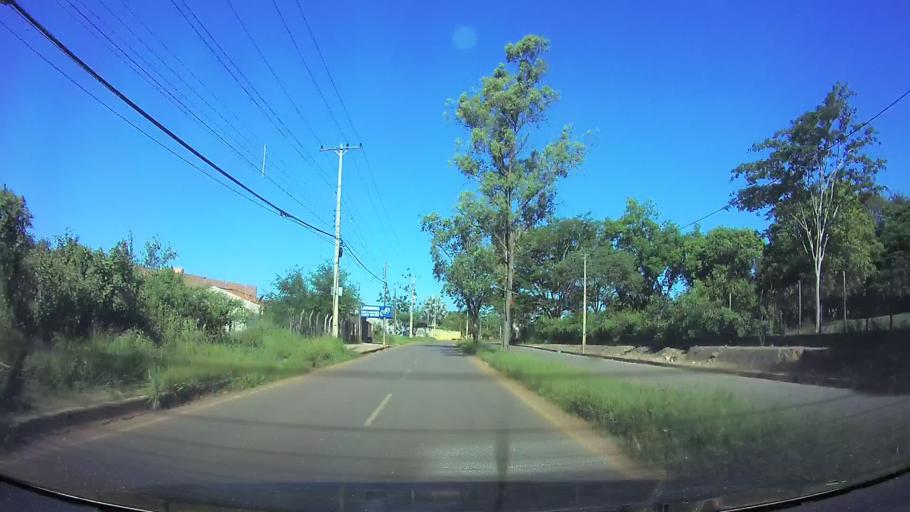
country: PY
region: Central
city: Fernando de la Mora
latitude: -25.2962
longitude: -57.5211
